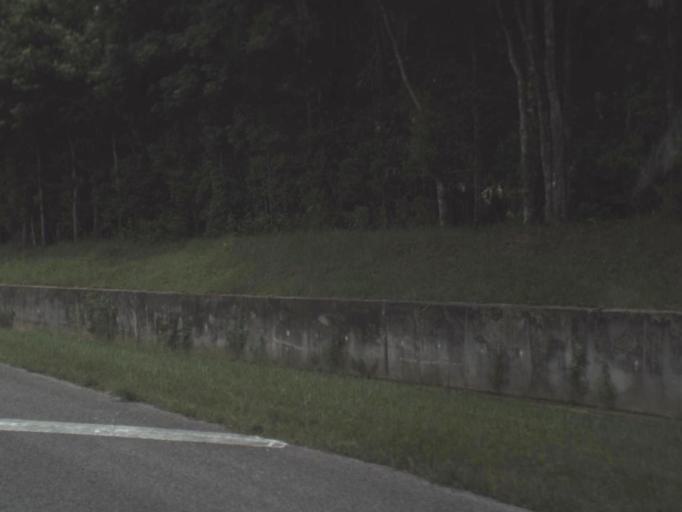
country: US
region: Florida
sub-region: Hernando County
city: North Brooksville
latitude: 28.5812
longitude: -82.4002
